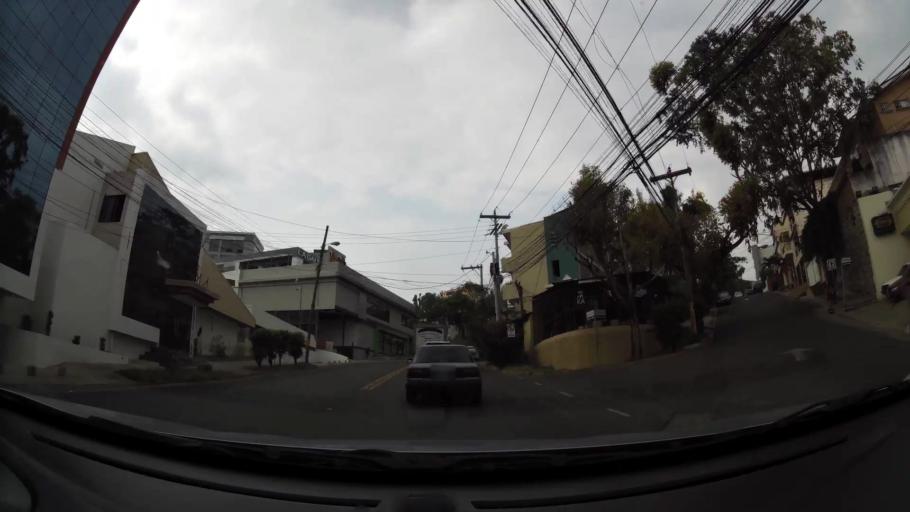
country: HN
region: Francisco Morazan
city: Tegucigalpa
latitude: 14.0971
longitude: -87.1847
